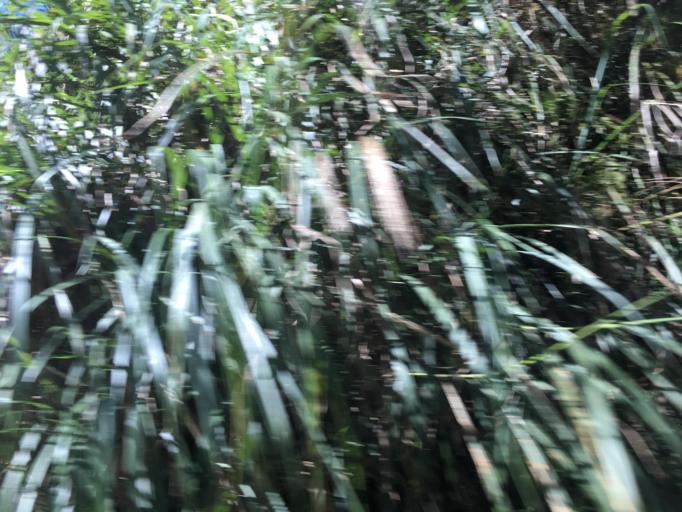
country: TW
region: Taiwan
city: Daxi
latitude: 24.5730
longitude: 121.4149
